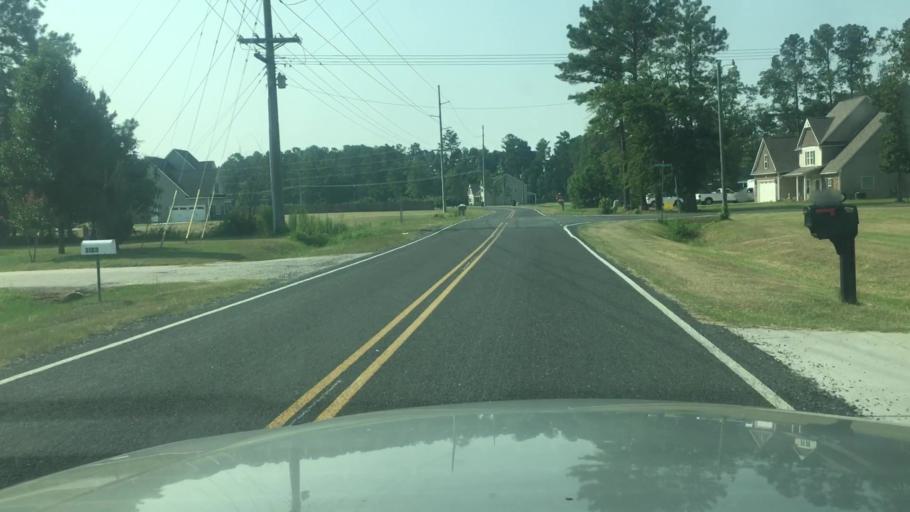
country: US
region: North Carolina
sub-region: Cumberland County
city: Hope Mills
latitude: 34.9037
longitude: -78.8719
